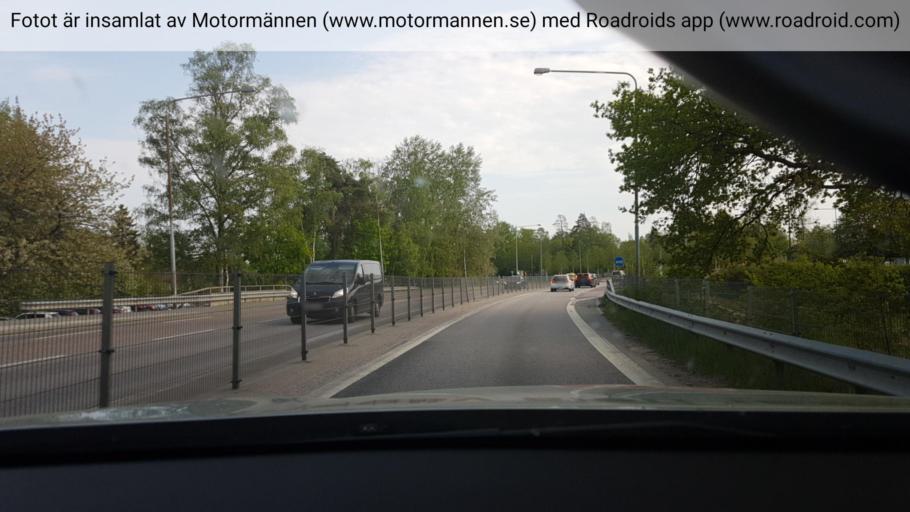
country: SE
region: Stockholm
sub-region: Tyreso Kommun
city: Bollmora
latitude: 59.2246
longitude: 18.2021
